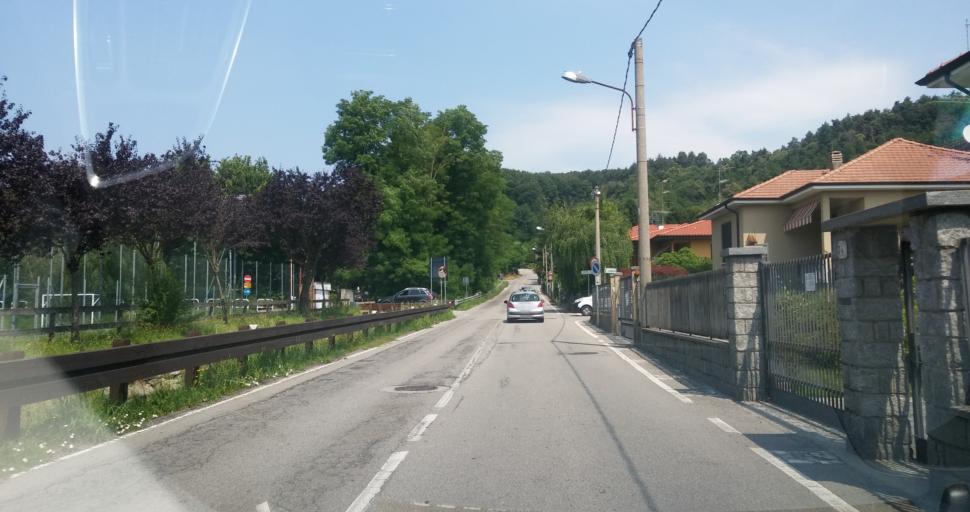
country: IT
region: Lombardy
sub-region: Provincia di Varese
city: Sesto Calende
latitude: 45.7320
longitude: 8.6319
